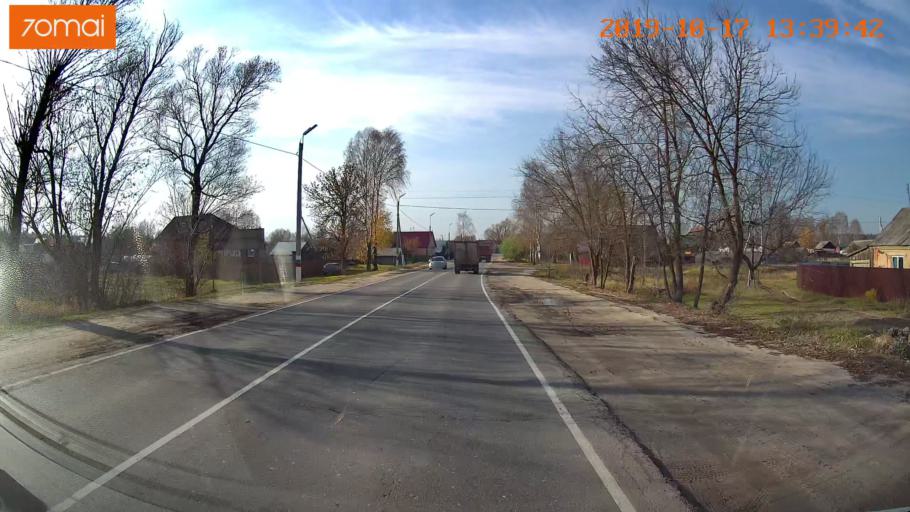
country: RU
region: Rjazan
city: Tuma
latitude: 55.1462
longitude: 40.5826
